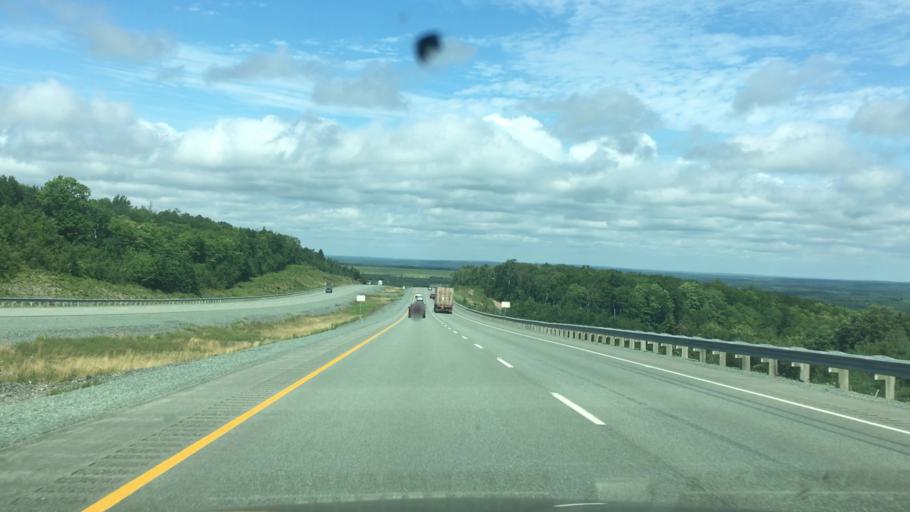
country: CA
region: Nova Scotia
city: Oxford
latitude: 45.5895
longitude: -63.7224
